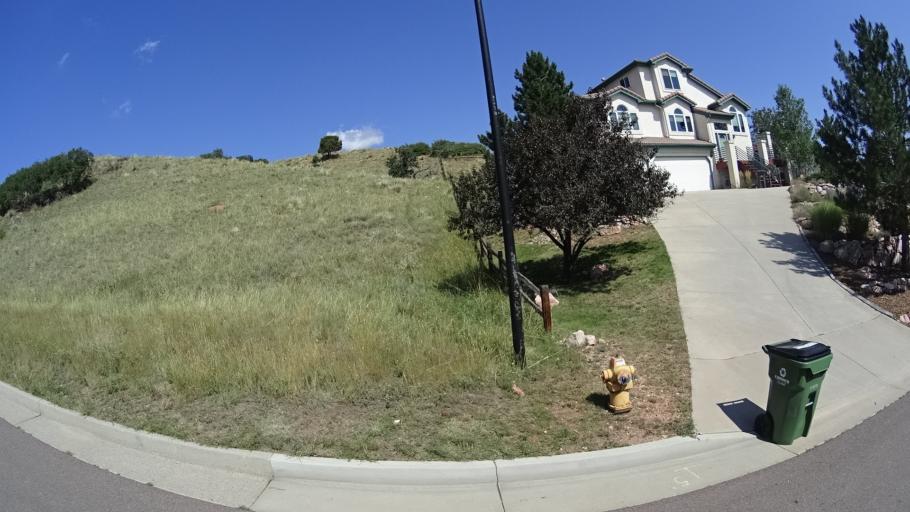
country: US
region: Colorado
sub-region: El Paso County
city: Air Force Academy
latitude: 38.9232
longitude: -104.8723
